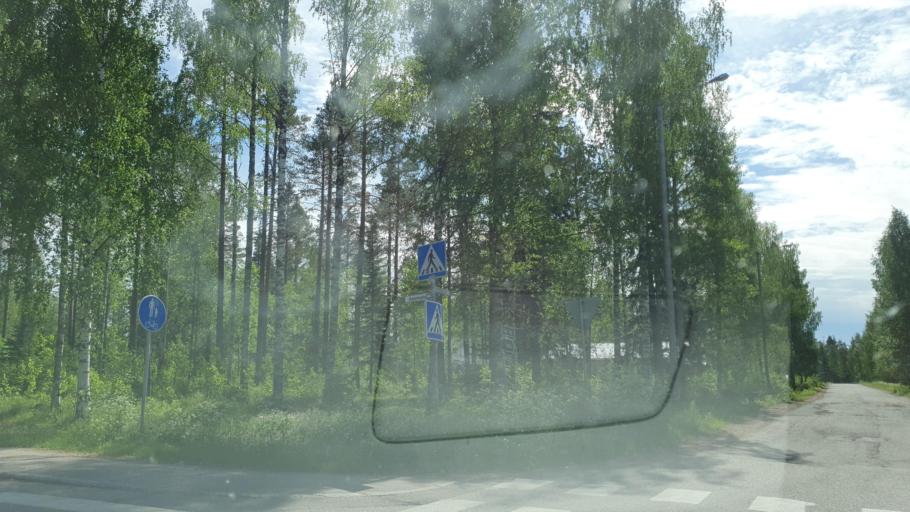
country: FI
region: Kainuu
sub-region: Kehys-Kainuu
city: Hyrynsalmi
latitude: 64.6833
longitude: 28.4636
